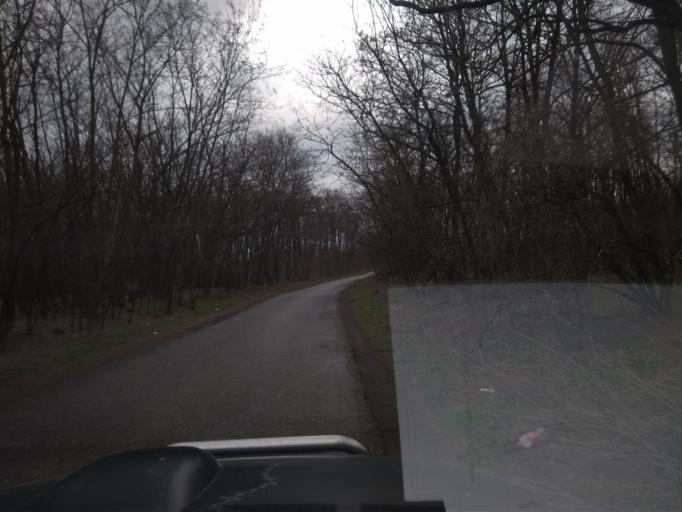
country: HU
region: Szabolcs-Szatmar-Bereg
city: Nyirpazony
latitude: 48.0222
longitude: 21.8046
